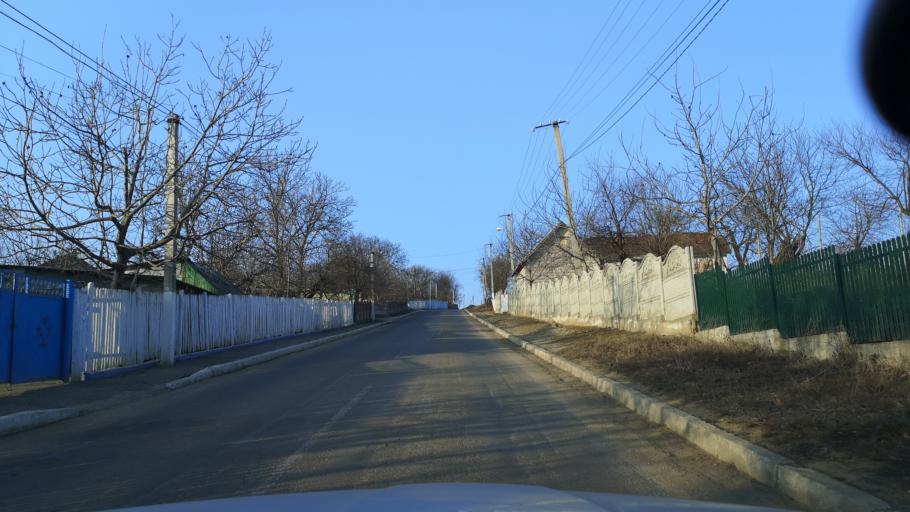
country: MD
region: Stinga Nistrului
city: Bucovat
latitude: 47.1208
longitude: 28.5041
